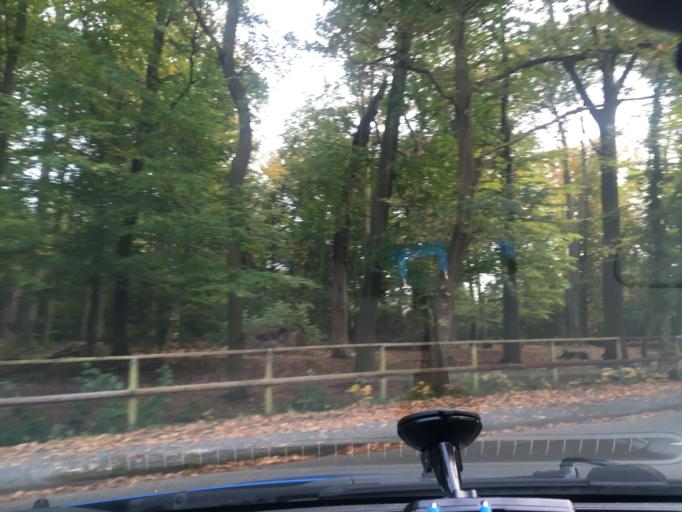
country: DE
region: Lower Saxony
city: Lueneburg
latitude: 53.2608
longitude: 10.4248
